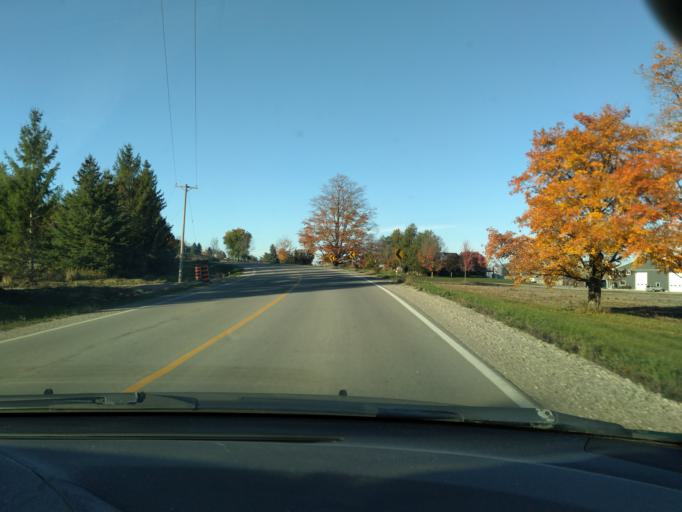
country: CA
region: Ontario
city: Bradford West Gwillimbury
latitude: 44.0574
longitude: -79.7363
